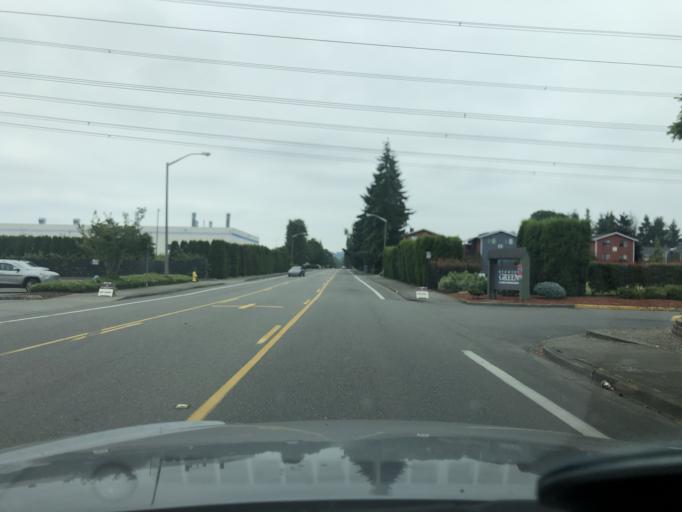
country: US
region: Washington
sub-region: King County
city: Auburn
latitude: 47.3366
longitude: -122.2193
